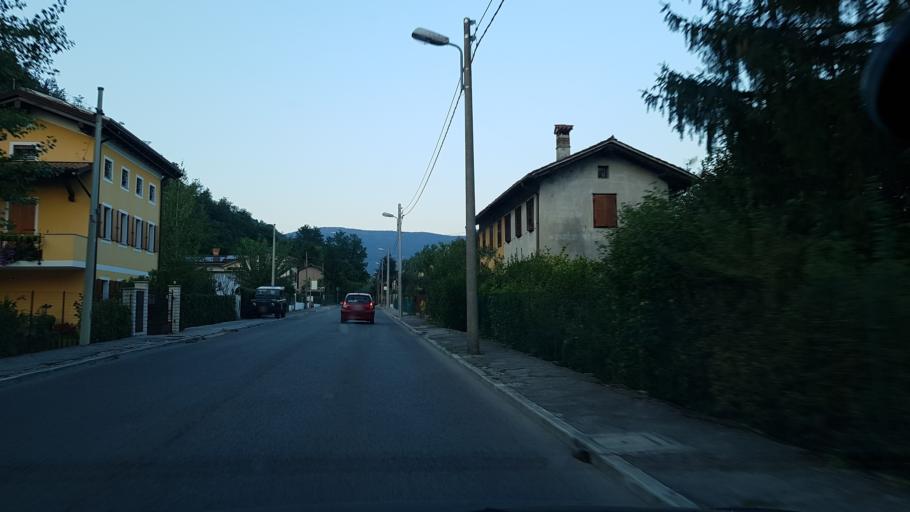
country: IT
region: Friuli Venezia Giulia
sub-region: Provincia di Gorizia
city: Gorizia
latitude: 45.9513
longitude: 13.6045
